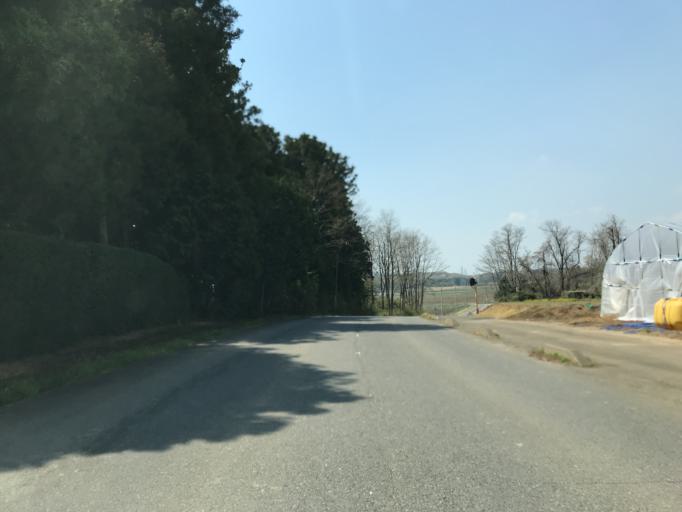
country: JP
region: Fukushima
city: Sukagawa
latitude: 37.1852
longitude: 140.3459
